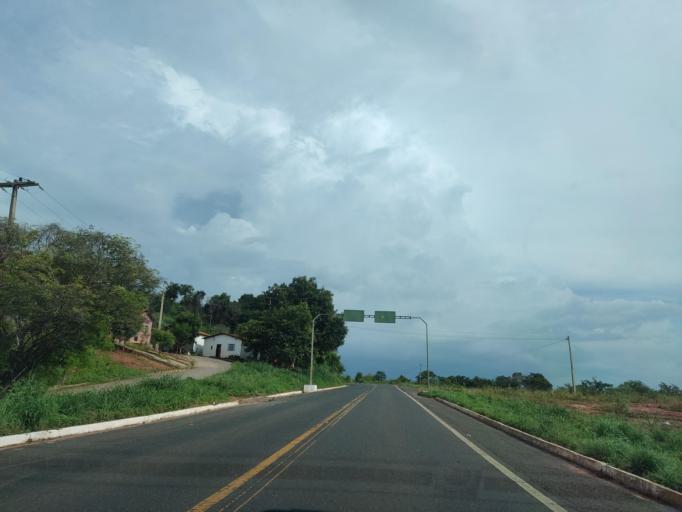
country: BR
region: Piaui
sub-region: Agua Branca
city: Agua Branca
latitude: -5.8237
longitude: -42.5060
